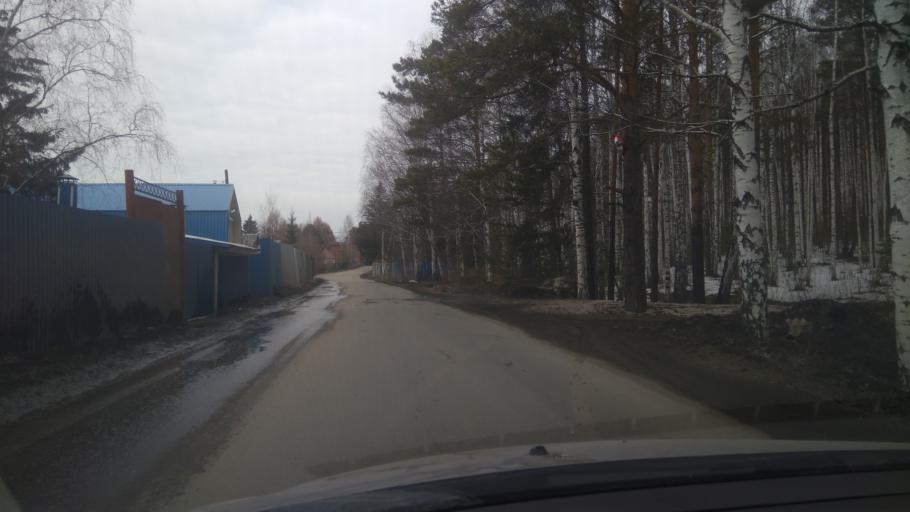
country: RU
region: Sverdlovsk
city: Severka
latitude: 56.8448
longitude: 60.3835
